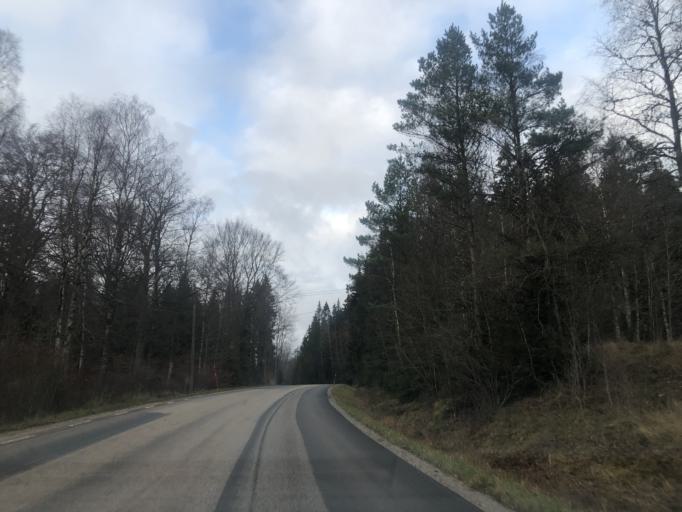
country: SE
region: Vaestra Goetaland
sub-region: Tranemo Kommun
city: Langhem
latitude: 57.7114
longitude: 13.2982
